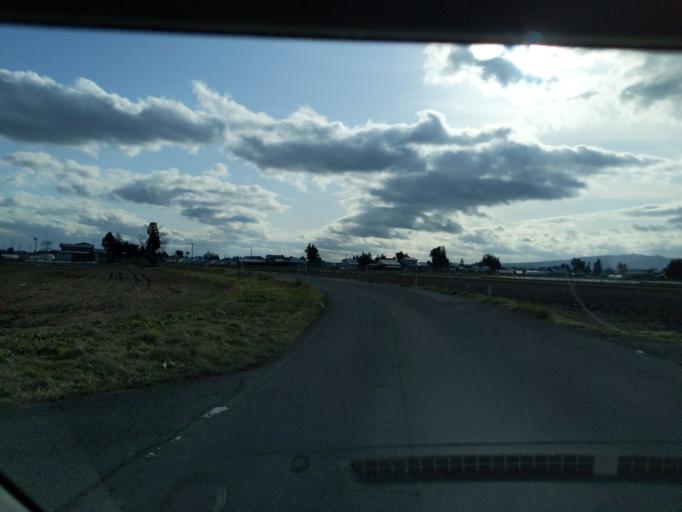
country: JP
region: Iwate
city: Mizusawa
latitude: 39.1510
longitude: 141.0784
